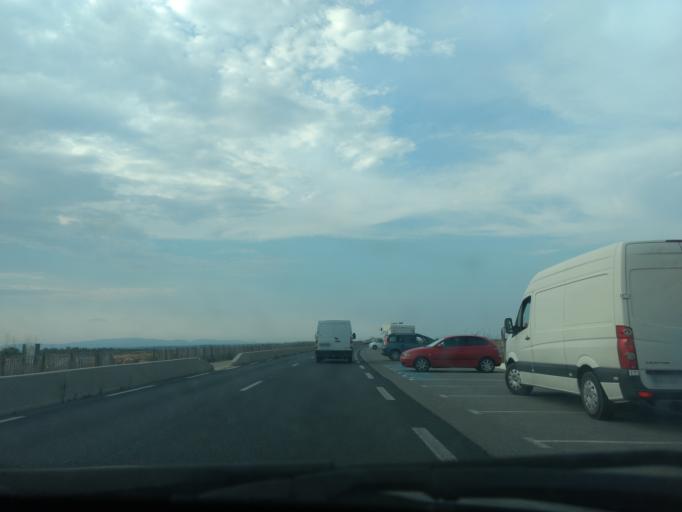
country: FR
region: Languedoc-Roussillon
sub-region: Departement des Pyrenees-Orientales
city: Saint-Cyprien-Plage
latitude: 42.6491
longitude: 3.0331
